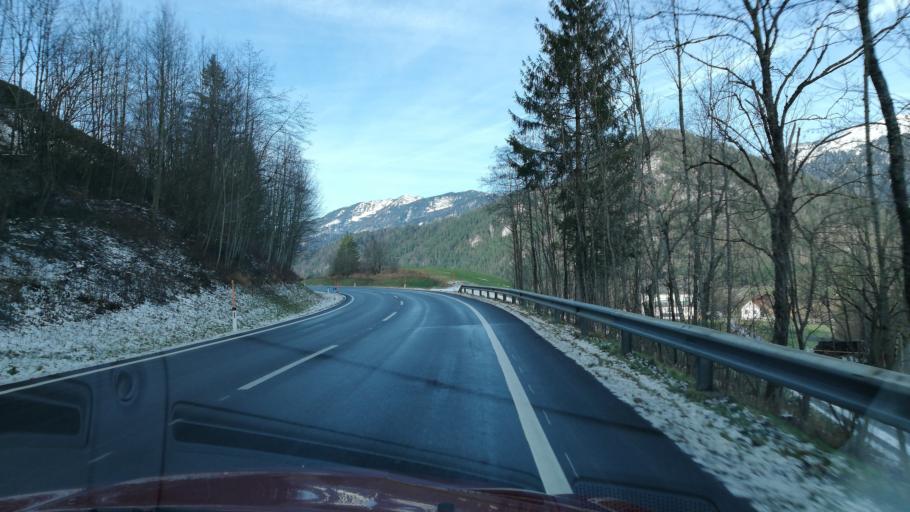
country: AT
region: Upper Austria
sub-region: Politischer Bezirk Kirchdorf an der Krems
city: Rossleithen
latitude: 47.7292
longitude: 14.2933
